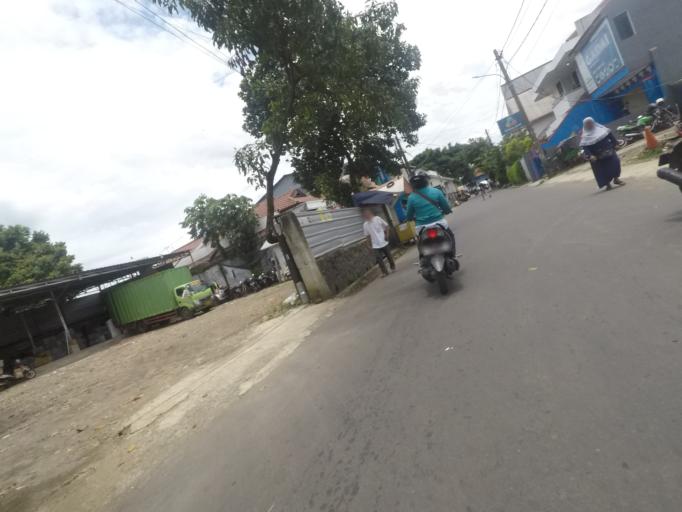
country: ID
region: West Java
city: Bogor
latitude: -6.5896
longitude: 106.7897
